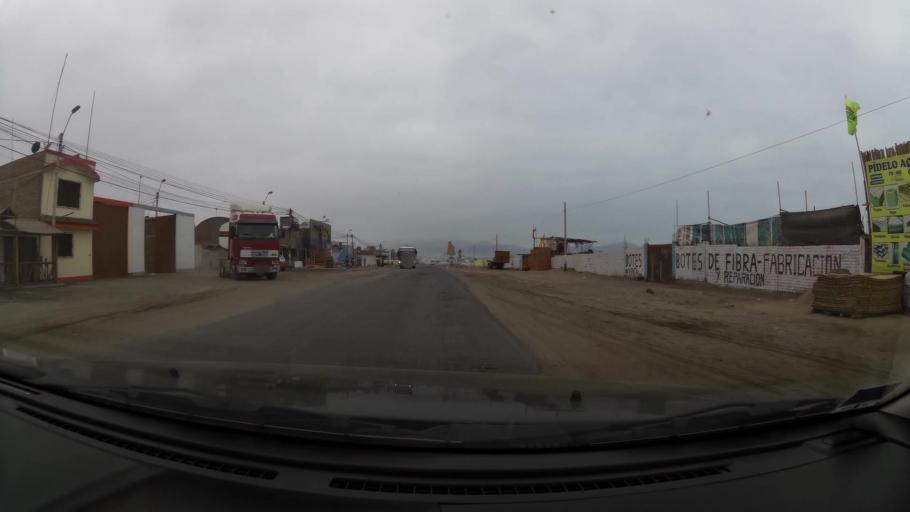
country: PE
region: Lima
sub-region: Lima
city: Punta Hermosa
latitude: -12.3491
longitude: -76.8118
